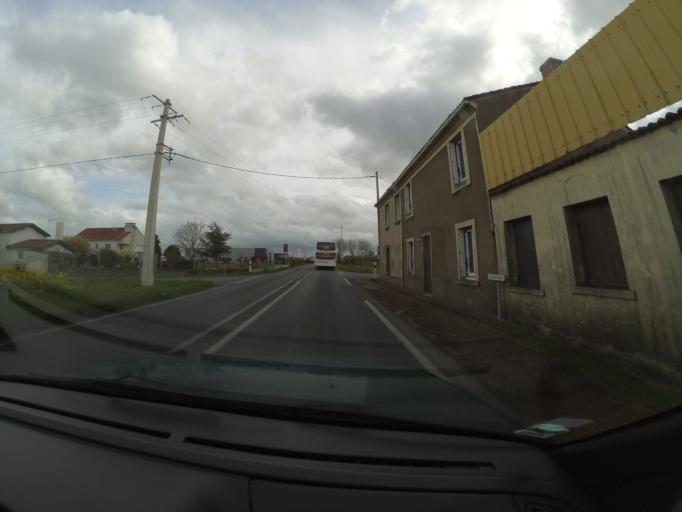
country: FR
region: Pays de la Loire
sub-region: Departement de Maine-et-Loire
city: Lire
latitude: 47.3265
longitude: -1.1666
